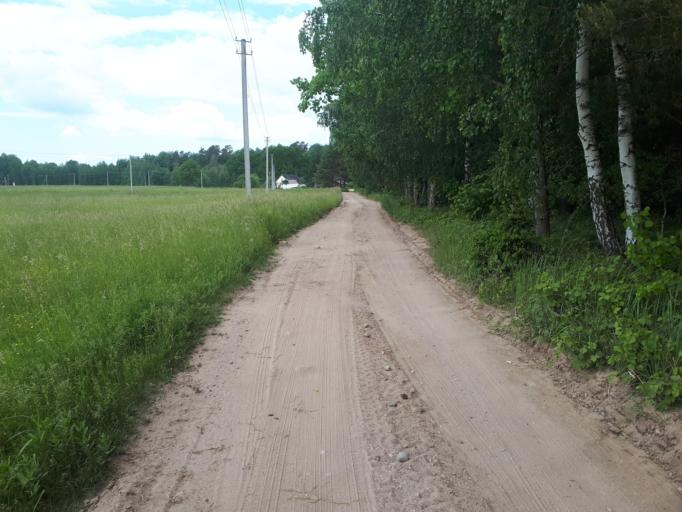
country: LT
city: Prienai
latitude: 54.6292
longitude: 23.9444
